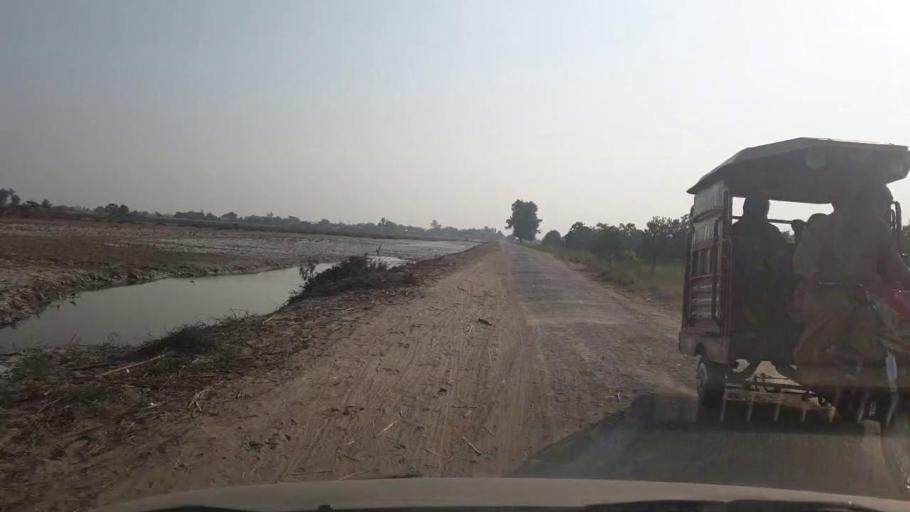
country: PK
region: Sindh
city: Digri
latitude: 25.2576
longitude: 69.1621
